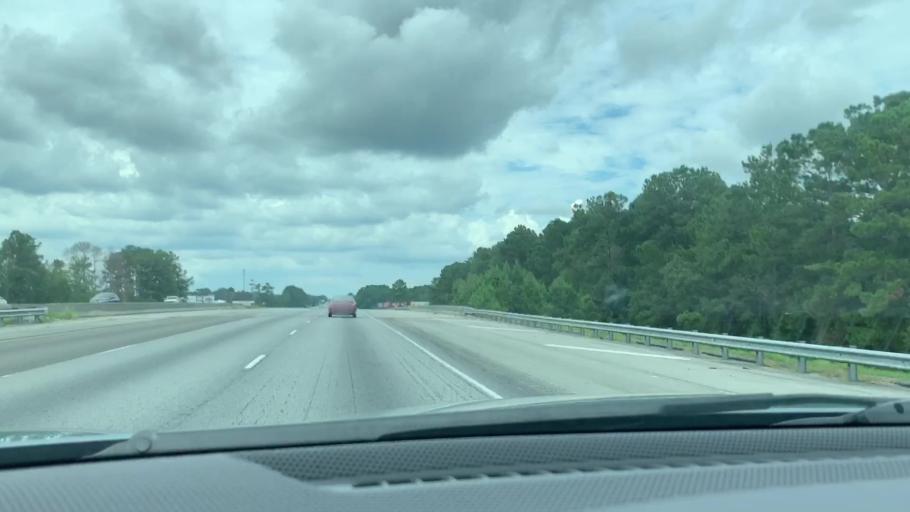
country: US
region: Georgia
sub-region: Bryan County
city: Richmond Hill
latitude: 31.9114
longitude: -81.3256
